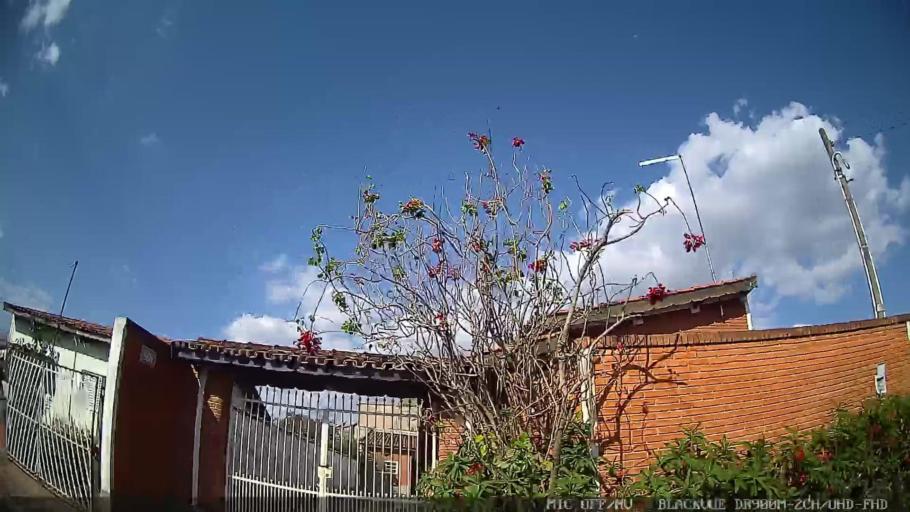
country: BR
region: Sao Paulo
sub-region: Cabreuva
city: Cabreuva
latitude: -23.2501
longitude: -47.0588
